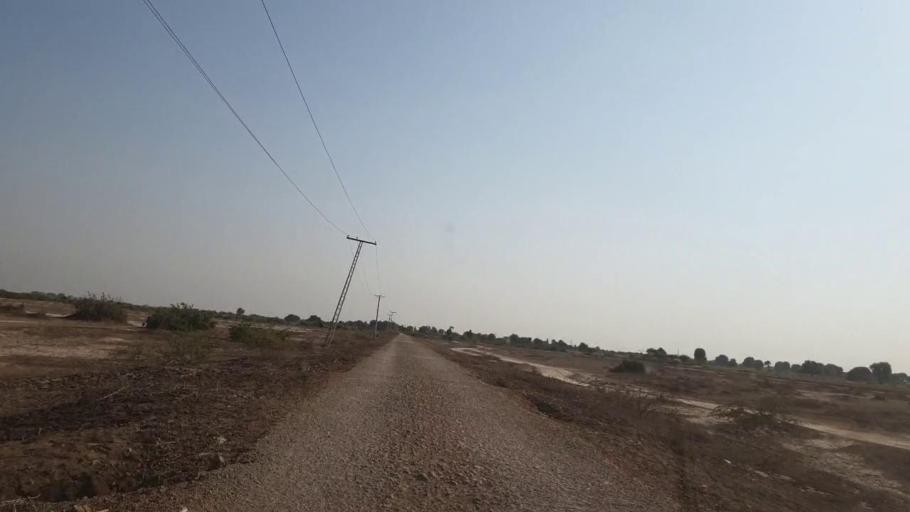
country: PK
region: Sindh
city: Naukot
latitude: 25.0160
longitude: 69.4746
